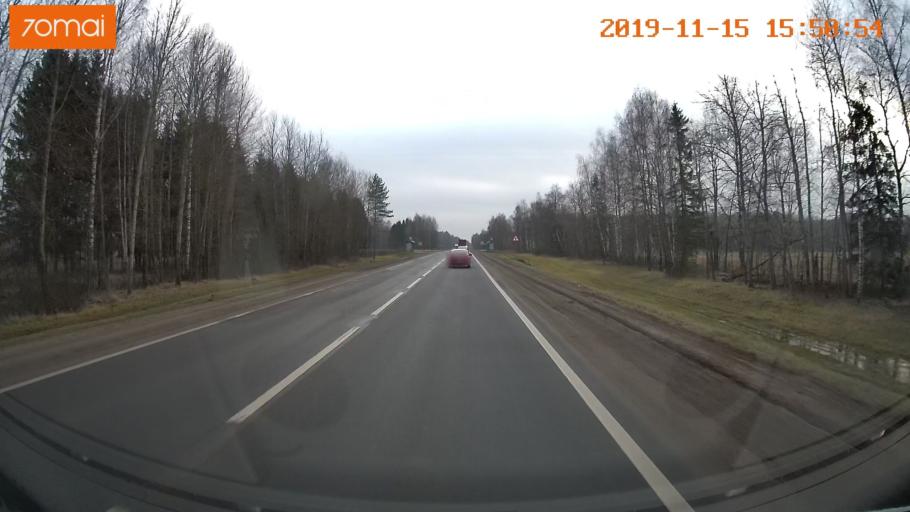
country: RU
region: Jaroslavl
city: Yaroslavl
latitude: 57.9008
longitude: 40.0114
